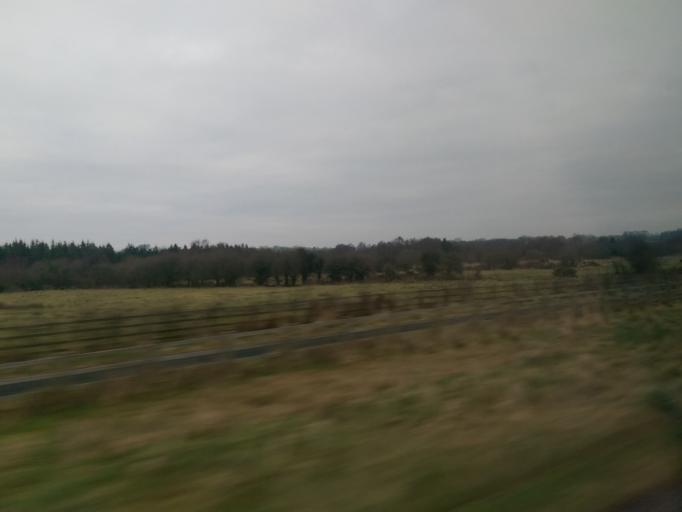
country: IE
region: Connaught
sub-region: County Galway
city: Ballinasloe
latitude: 53.3083
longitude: -8.3055
